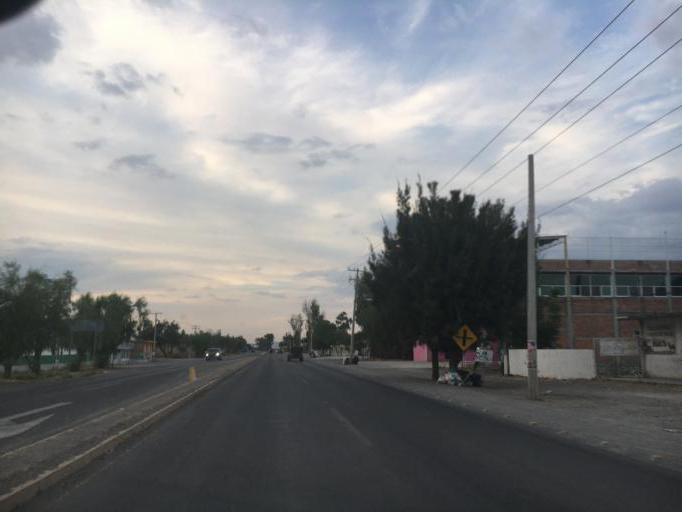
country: MX
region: Guanajuato
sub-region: Leon
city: El CERESO
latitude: 20.9935
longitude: -101.7028
